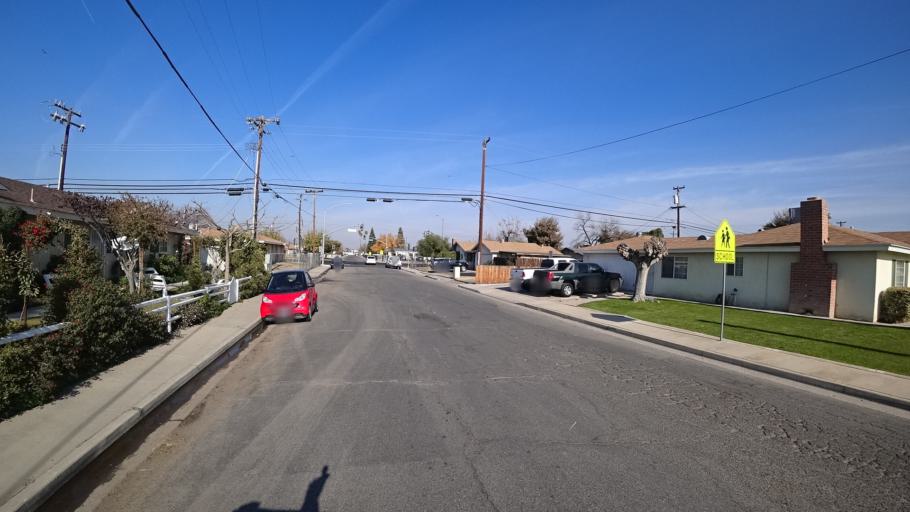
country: US
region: California
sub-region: Kern County
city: Greenfield
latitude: 35.3169
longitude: -119.0145
